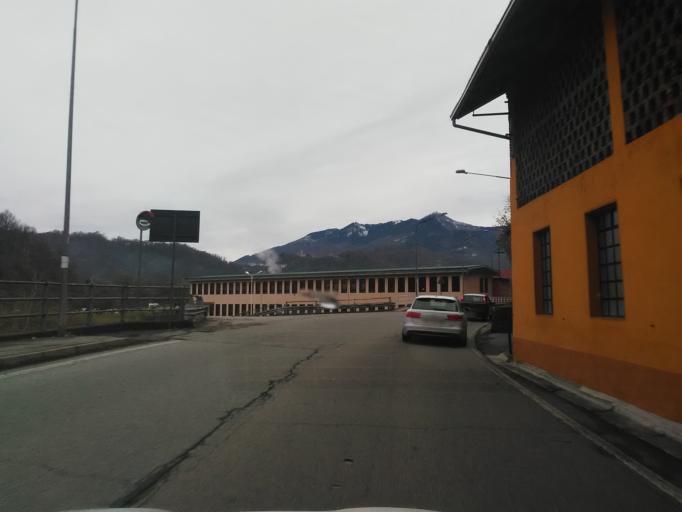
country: IT
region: Piedmont
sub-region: Provincia di Biella
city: Pray
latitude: 45.6744
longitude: 8.2204
